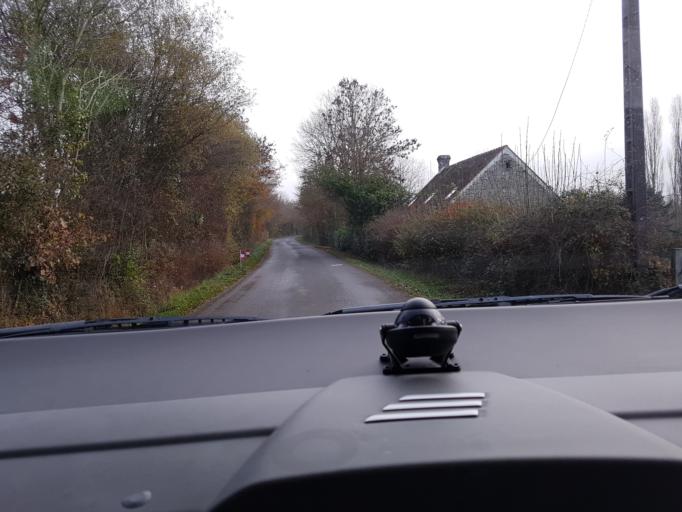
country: FR
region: Lower Normandy
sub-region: Departement de l'Orne
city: Ecouche
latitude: 48.6360
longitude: -0.0507
